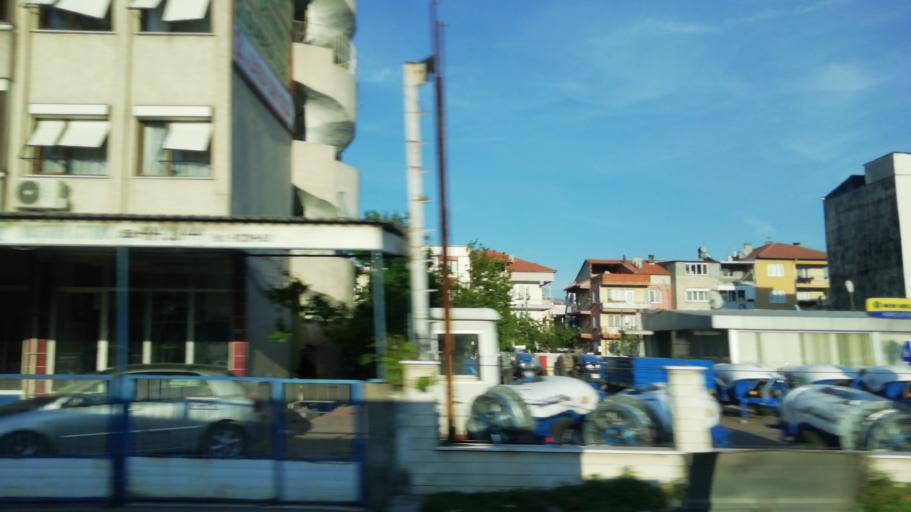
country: TR
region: Manisa
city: Akhisar
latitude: 38.9292
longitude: 27.8345
